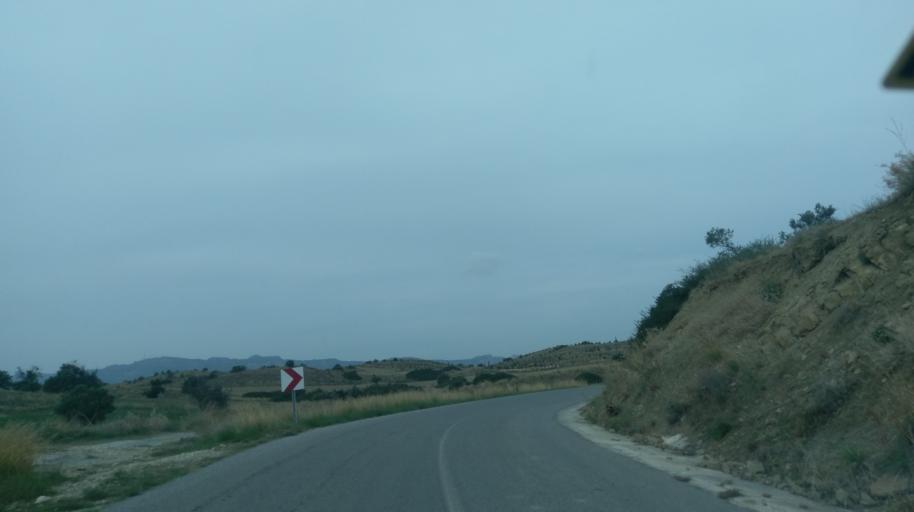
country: CY
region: Ammochostos
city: Trikomo
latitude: 35.3420
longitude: 33.9294
